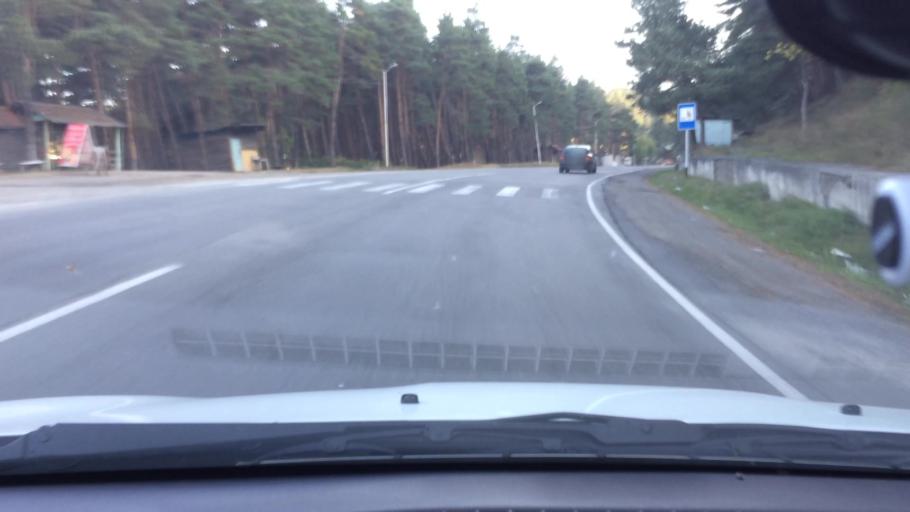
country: GE
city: Surami
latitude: 42.0211
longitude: 43.5656
